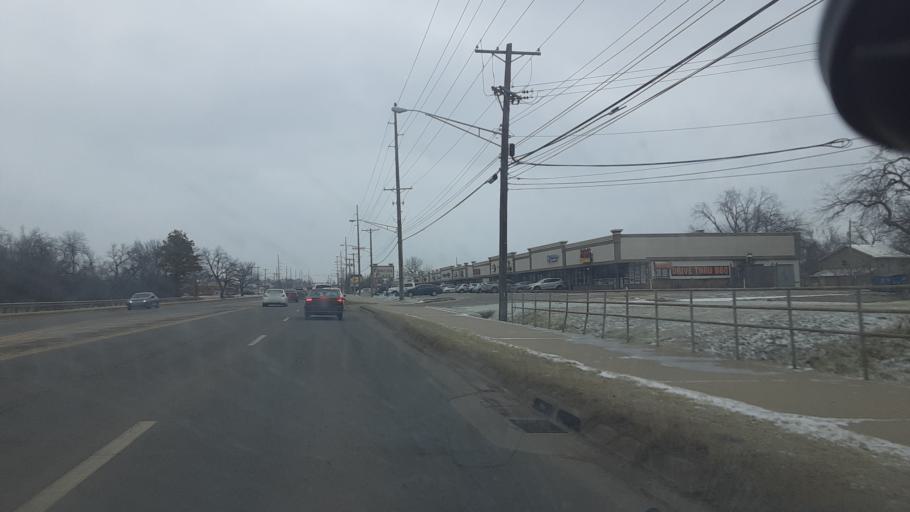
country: US
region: Oklahoma
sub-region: Payne County
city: Stillwater
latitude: 36.1194
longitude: -97.0513
